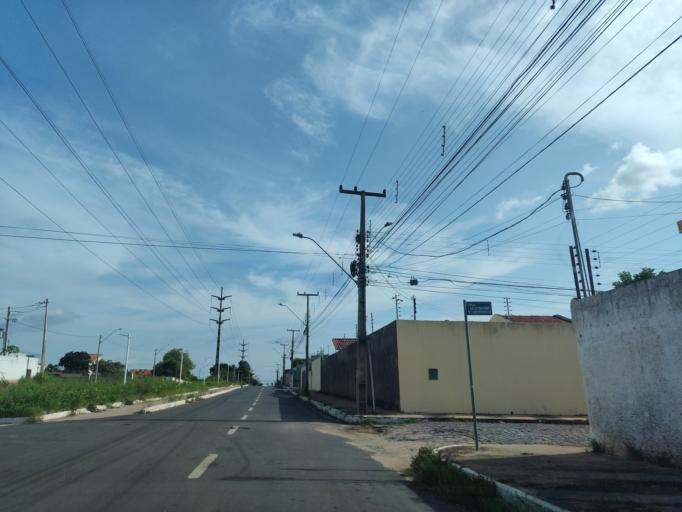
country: BR
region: Piaui
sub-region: Teresina
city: Teresina
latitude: -5.0683
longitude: -42.7516
